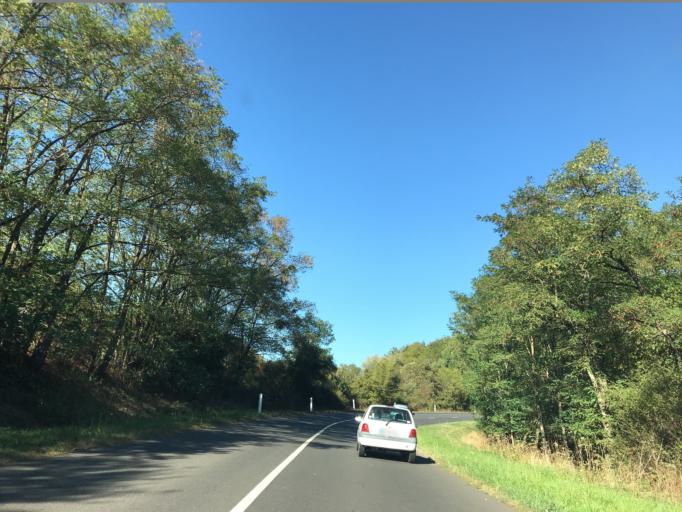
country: FR
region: Auvergne
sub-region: Departement du Puy-de-Dome
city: Peschadoires
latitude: 45.7868
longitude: 3.4538
